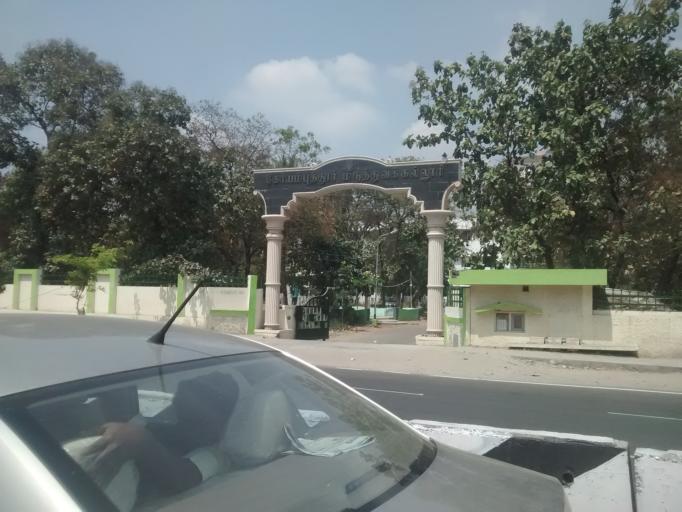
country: IN
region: Tamil Nadu
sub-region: Coimbatore
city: Singanallur
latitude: 11.0279
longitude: 77.0244
